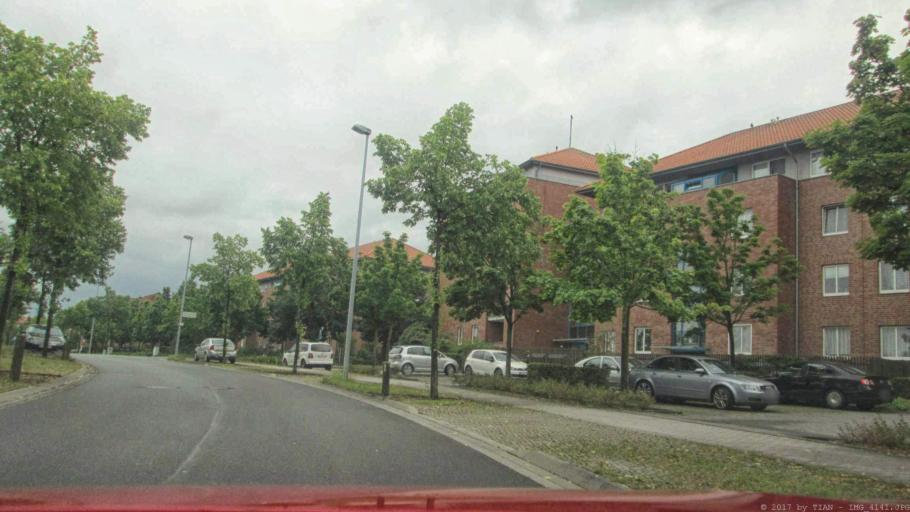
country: DE
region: Lower Saxony
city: Wolfsburg
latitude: 52.4155
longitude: 10.8324
